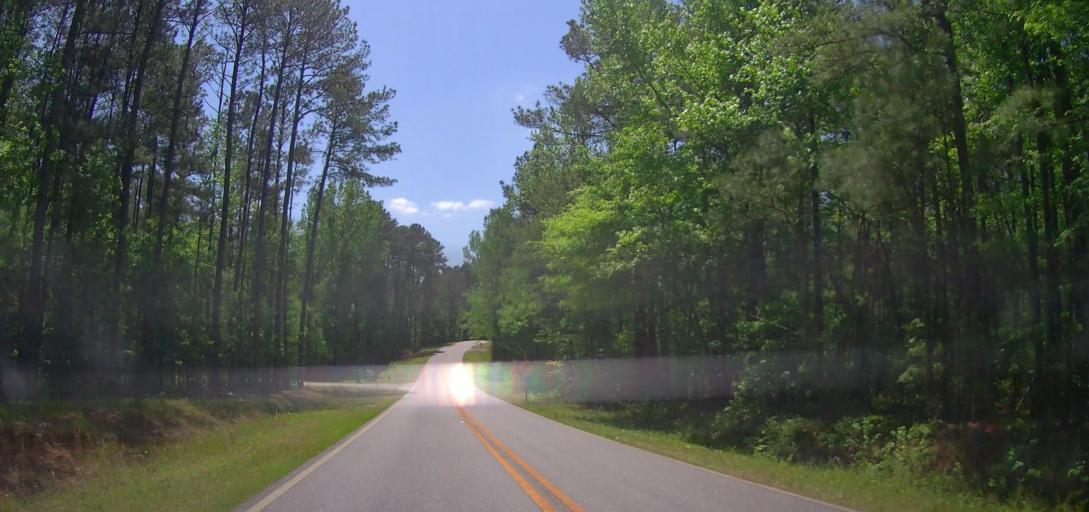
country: US
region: Georgia
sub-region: Jones County
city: Gray
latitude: 32.9638
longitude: -83.5567
